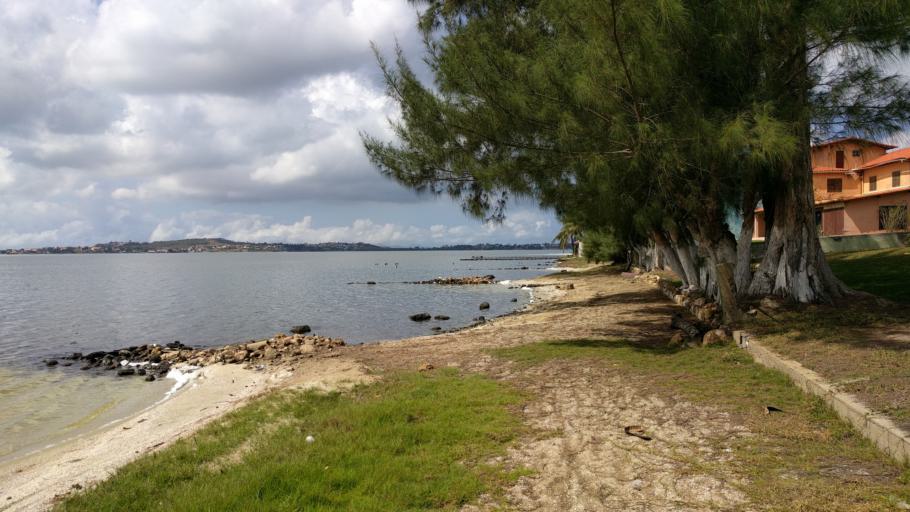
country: BR
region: Rio de Janeiro
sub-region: Sao Pedro Da Aldeia
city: Sao Pedro da Aldeia
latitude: -22.8410
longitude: -42.1267
